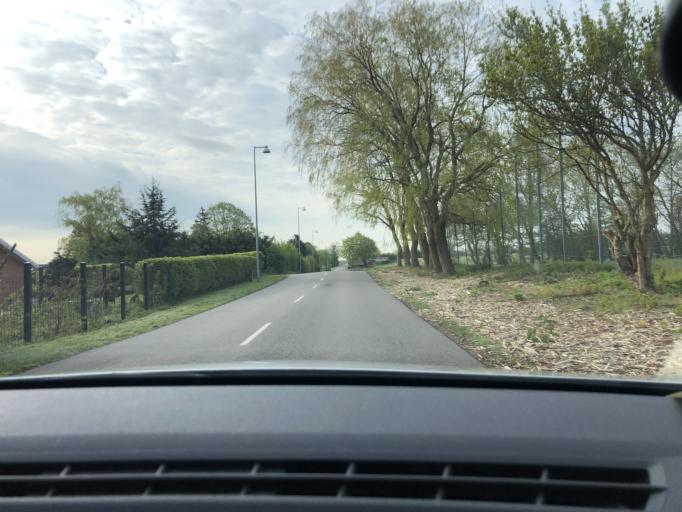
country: DK
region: Zealand
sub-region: Faxe Kommune
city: Ronnede
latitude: 55.2405
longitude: 12.0450
